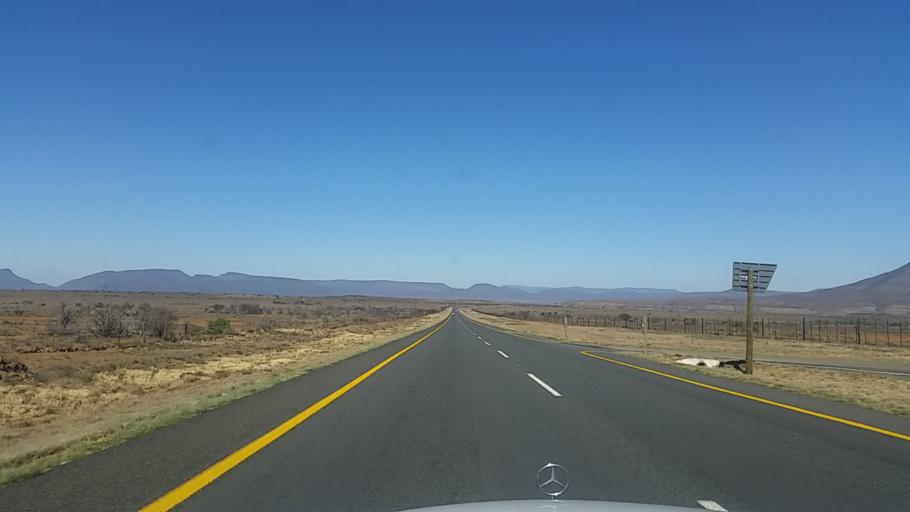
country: ZA
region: Eastern Cape
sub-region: Cacadu District Municipality
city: Graaff-Reinet
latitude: -32.1236
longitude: 24.5993
